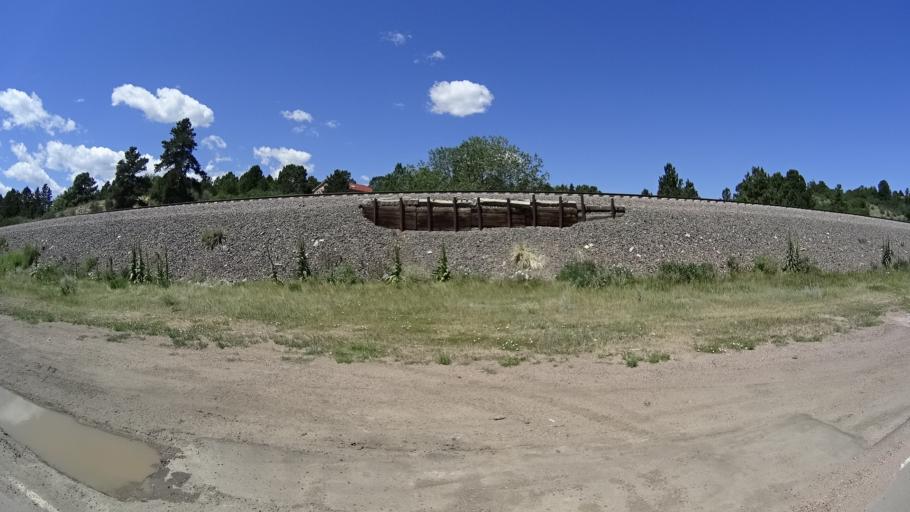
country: US
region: Colorado
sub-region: El Paso County
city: Air Force Academy
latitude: 38.9219
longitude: -104.8198
